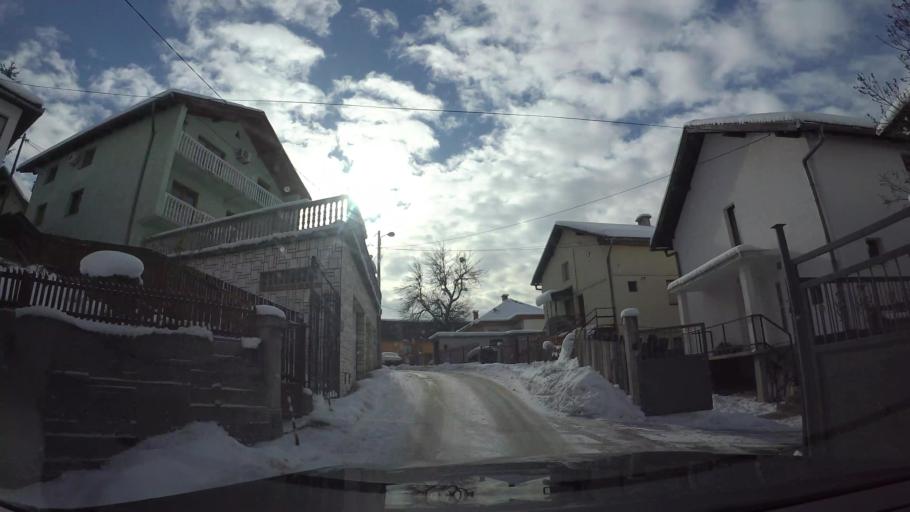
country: BA
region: Federation of Bosnia and Herzegovina
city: Kobilja Glava
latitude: 43.8787
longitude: 18.4173
